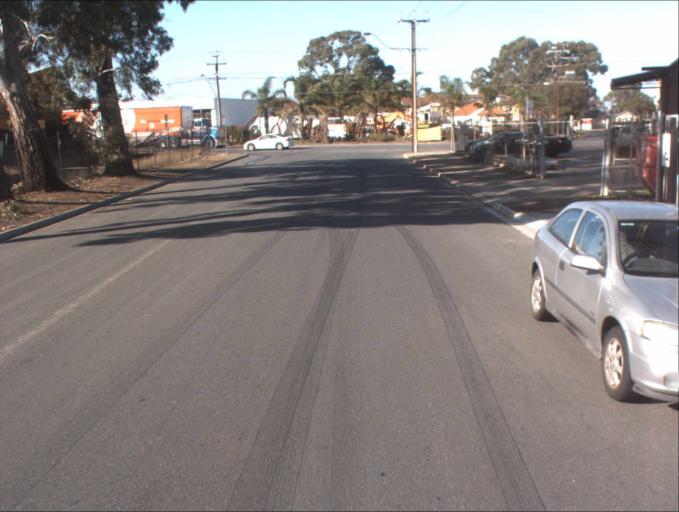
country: AU
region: South Australia
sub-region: Charles Sturt
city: Woodville North
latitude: -34.8496
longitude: 138.5551
